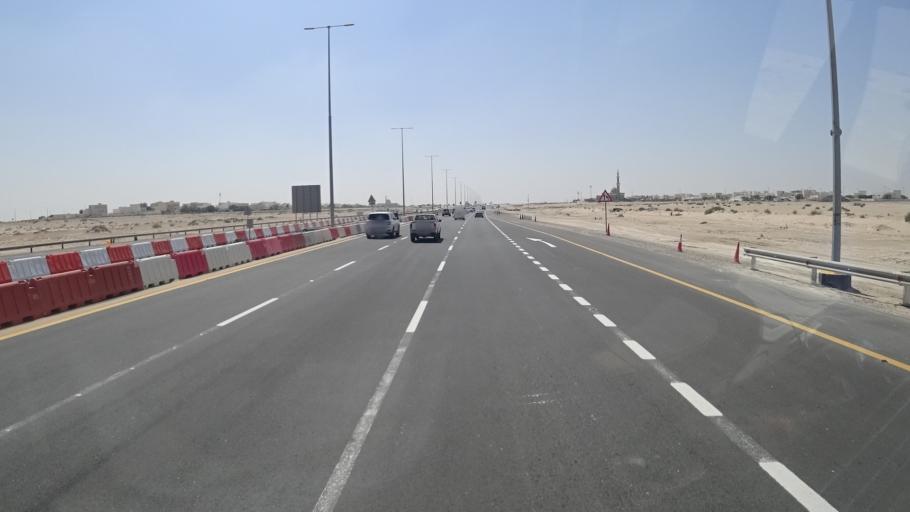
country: AE
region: Abu Dhabi
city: Abu Dhabi
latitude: 24.3362
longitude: 54.6981
